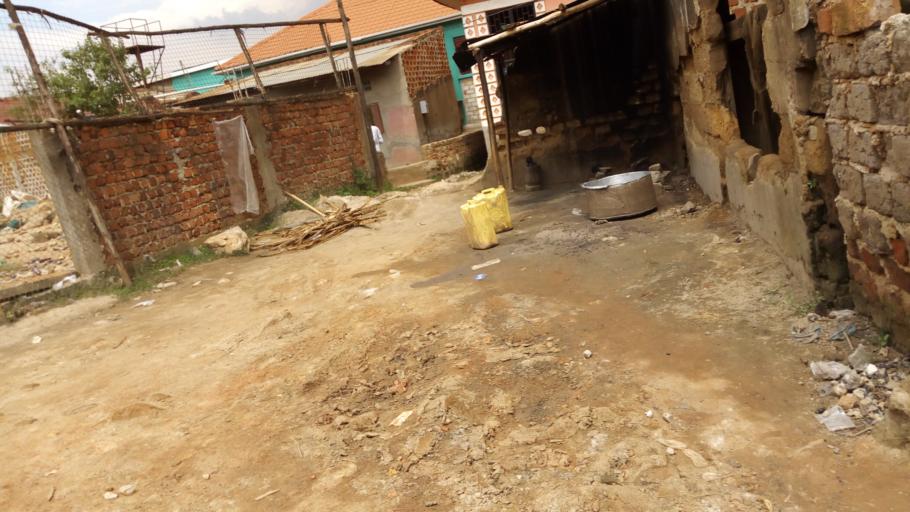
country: UG
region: Central Region
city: Kampala Central Division
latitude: 0.3513
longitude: 32.5616
